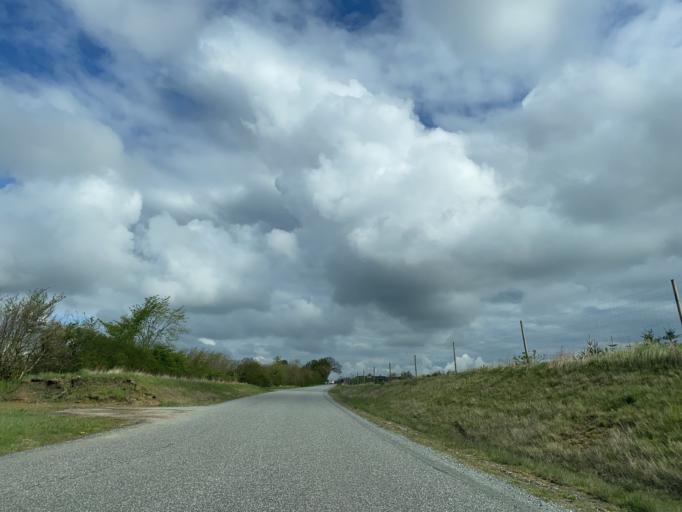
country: DK
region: Central Jutland
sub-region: Silkeborg Kommune
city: Silkeborg
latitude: 56.2113
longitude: 9.5179
